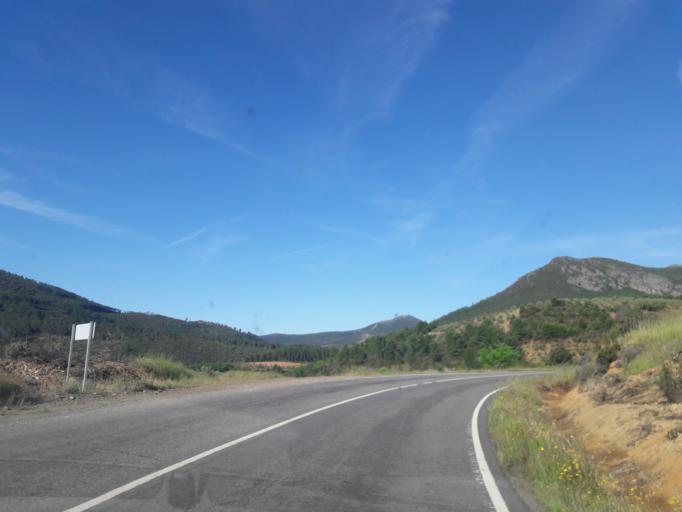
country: ES
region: Castille and Leon
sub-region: Provincia de Salamanca
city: Sotoserrano
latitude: 40.4148
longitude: -6.0377
